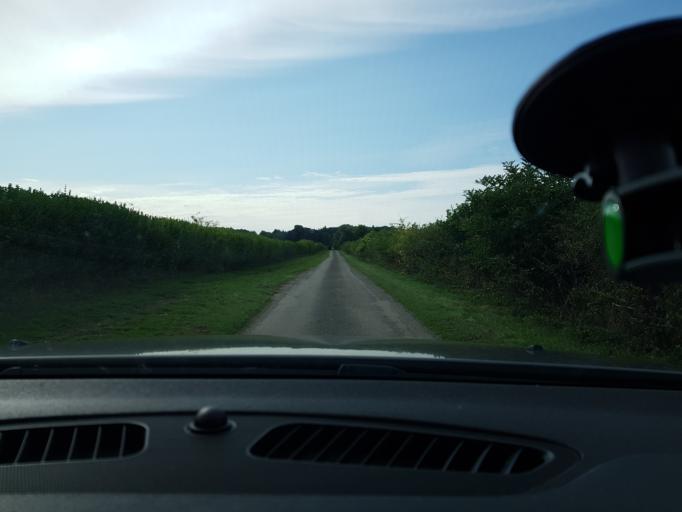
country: GB
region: England
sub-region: West Berkshire
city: Hungerford
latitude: 51.4011
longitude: -1.4841
